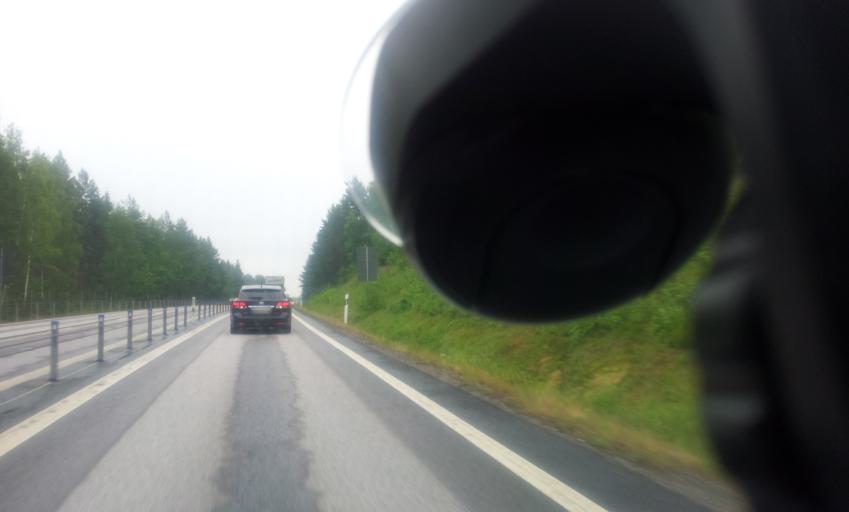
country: SE
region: Kalmar
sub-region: Vasterviks Kommun
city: Gamleby
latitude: 57.8247
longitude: 16.4576
